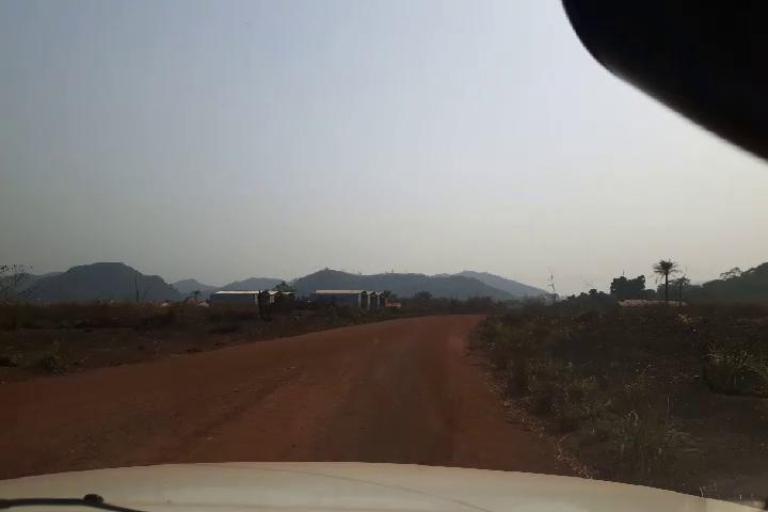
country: SL
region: Northern Province
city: Masingbi
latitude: 8.8574
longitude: -11.8220
